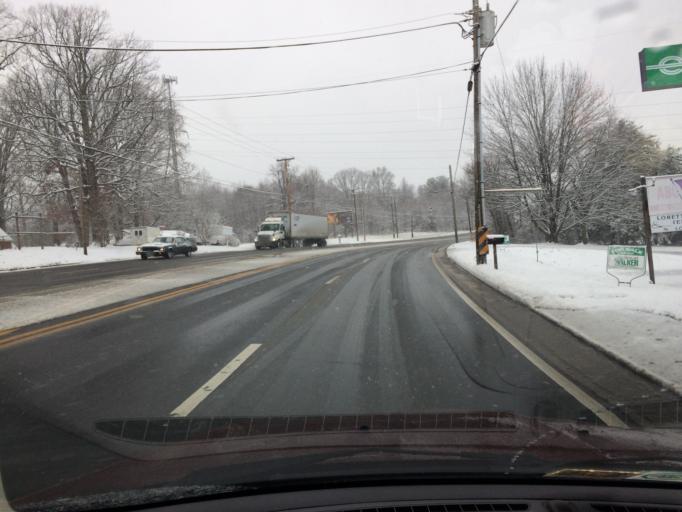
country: US
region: Virginia
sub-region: Amherst County
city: Madison Heights
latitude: 37.4536
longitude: -79.1219
